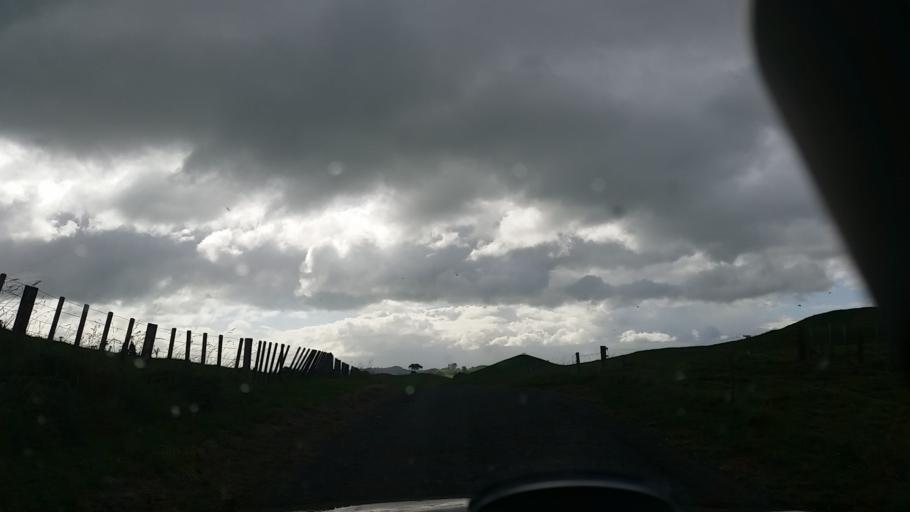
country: NZ
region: Waikato
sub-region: Matamata-Piako District
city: Matamata
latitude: -37.8227
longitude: 175.6756
